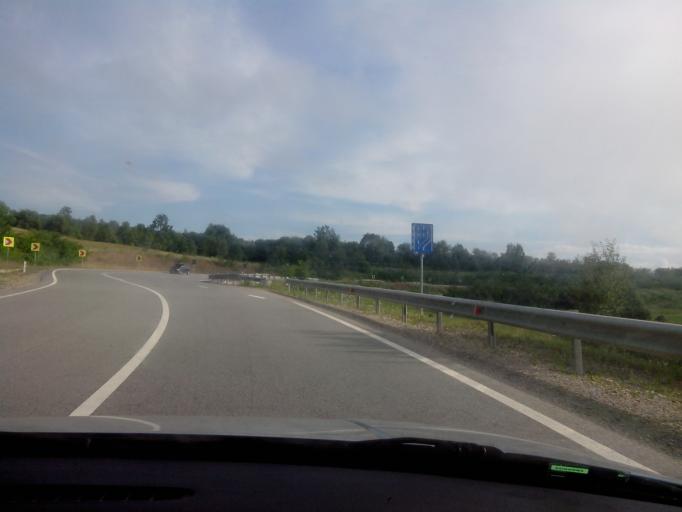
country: RO
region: Maramures
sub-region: Comuna Boiu Mare
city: Boiu Mare
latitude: 47.3757
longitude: 23.5342
